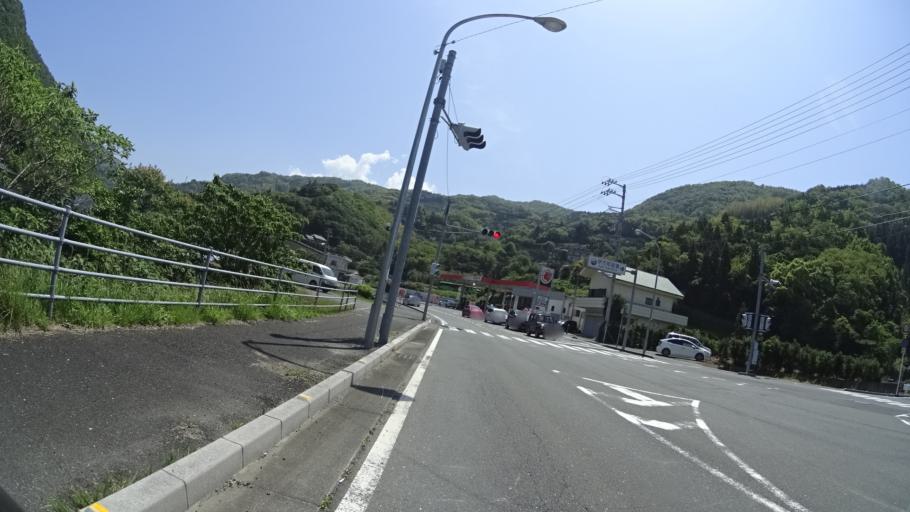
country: JP
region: Ehime
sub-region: Nishiuwa-gun
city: Ikata-cho
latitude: 33.4928
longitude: 132.3619
